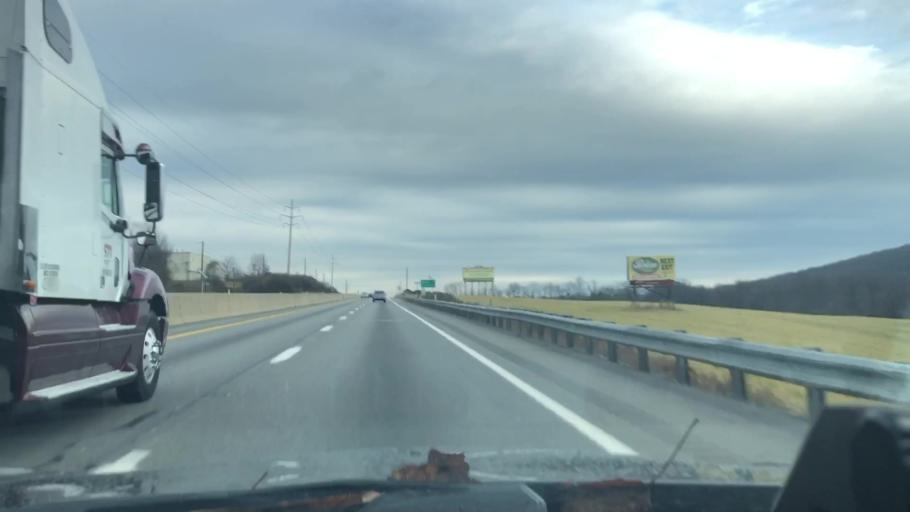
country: US
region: Pennsylvania
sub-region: Northampton County
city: Bethlehem
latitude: 40.6675
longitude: -75.3742
